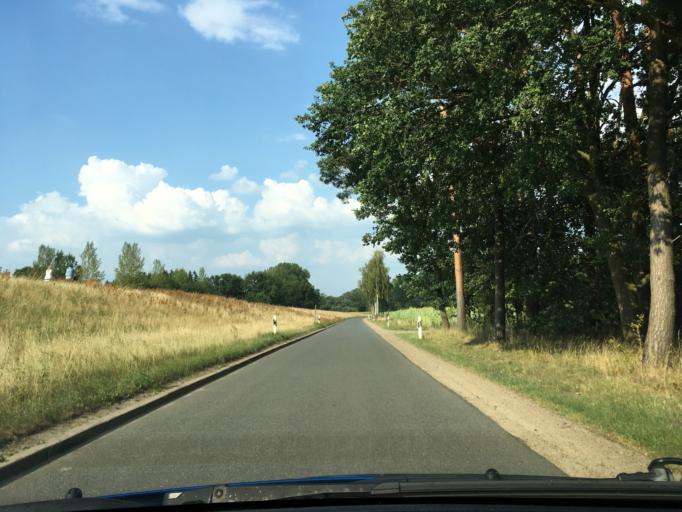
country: DE
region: Lower Saxony
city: Damnatz
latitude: 53.1582
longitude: 11.1311
